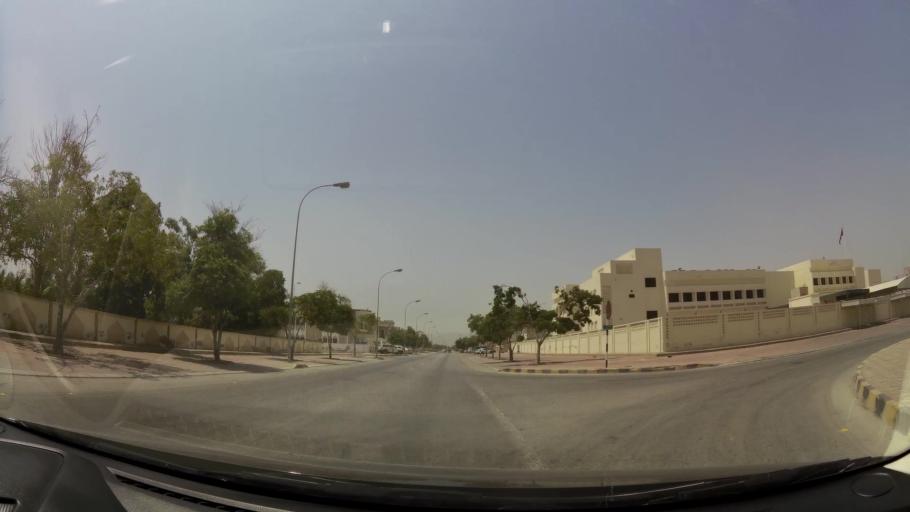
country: OM
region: Zufar
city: Salalah
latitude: 17.0142
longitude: 54.0757
